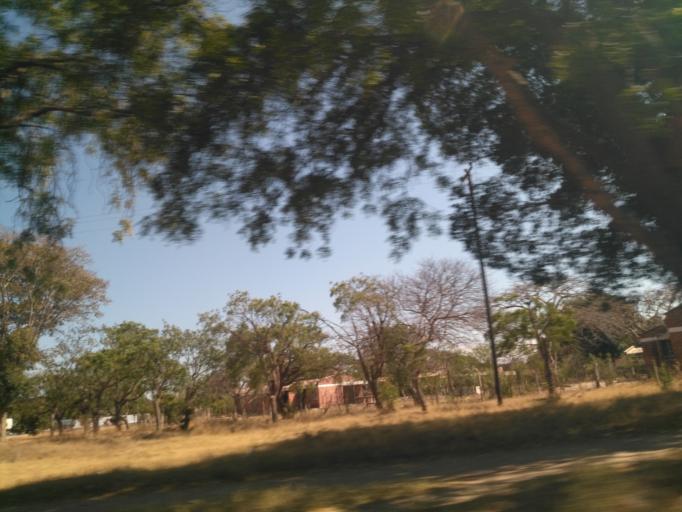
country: TZ
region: Dodoma
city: Dodoma
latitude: -6.1694
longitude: 35.7441
